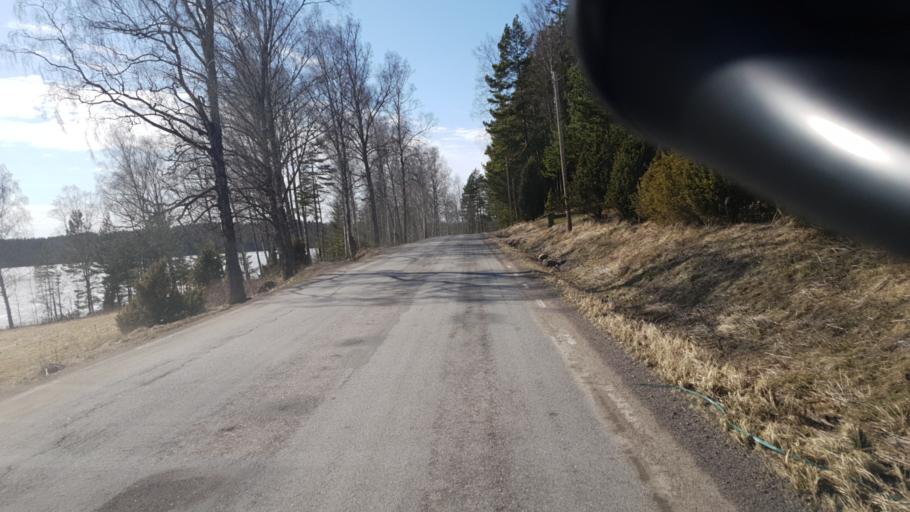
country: SE
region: Vaermland
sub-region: Arvika Kommun
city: Arvika
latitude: 59.6619
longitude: 12.7019
